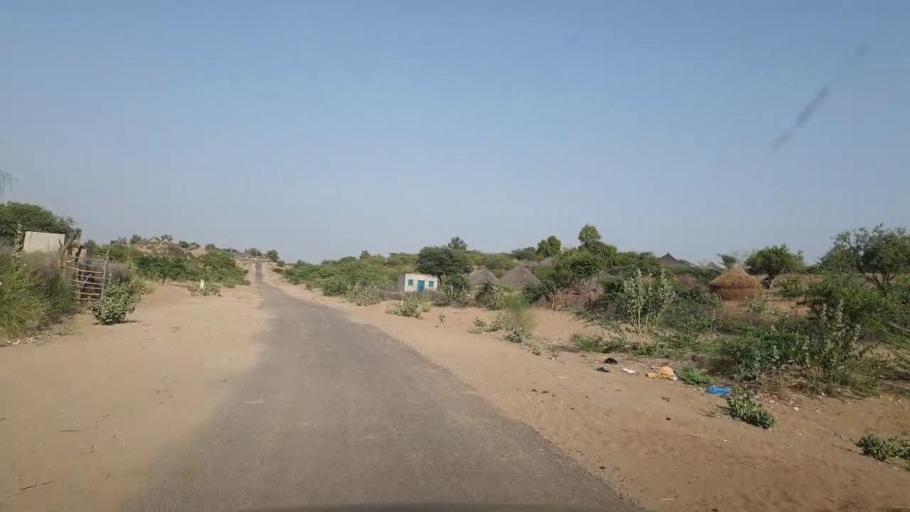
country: PK
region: Sindh
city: Islamkot
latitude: 25.1598
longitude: 70.5264
